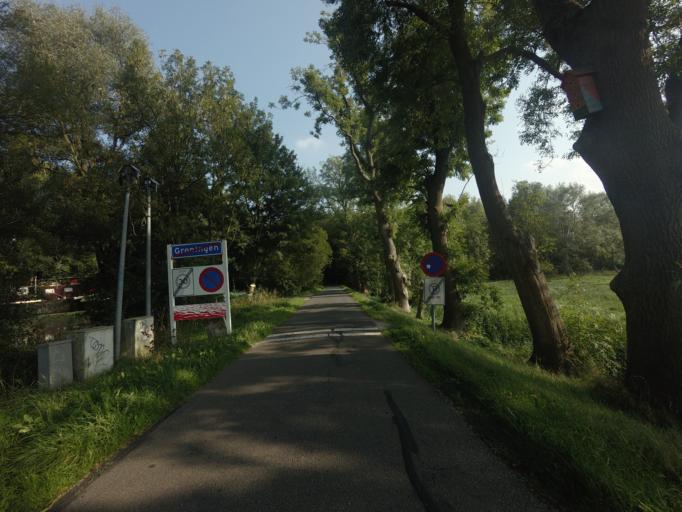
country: NL
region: Groningen
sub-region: Gemeente Groningen
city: Groningen
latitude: 53.1846
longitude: 6.5665
